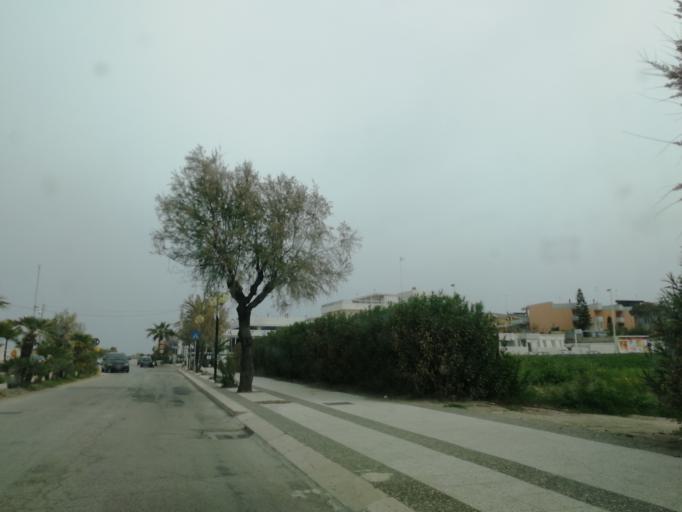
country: IT
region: Apulia
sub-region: Provincia di Barletta - Andria - Trani
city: Barletta
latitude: 41.3199
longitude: 16.2986
